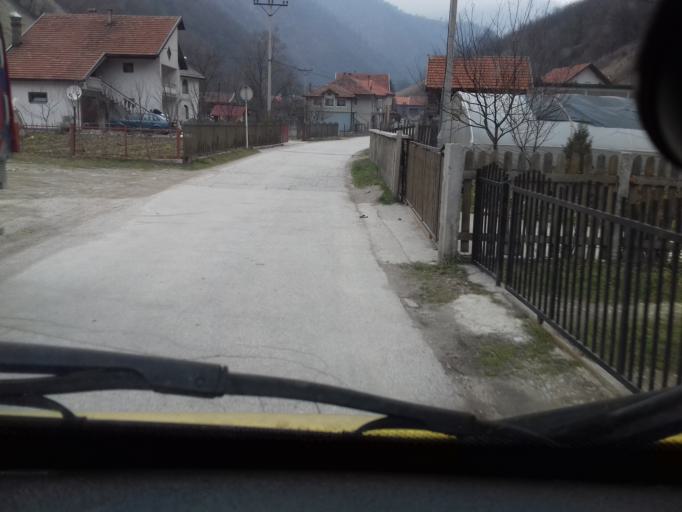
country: BA
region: Federation of Bosnia and Herzegovina
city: Zenica
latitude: 44.2479
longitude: 17.9208
